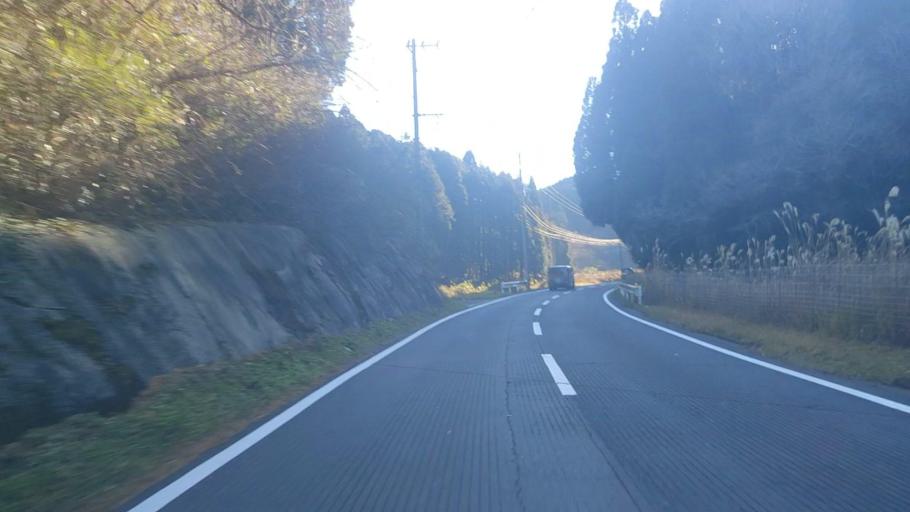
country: JP
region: Saga Prefecture
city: Kanzakimachi-kanzaki
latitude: 33.4180
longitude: 130.2792
